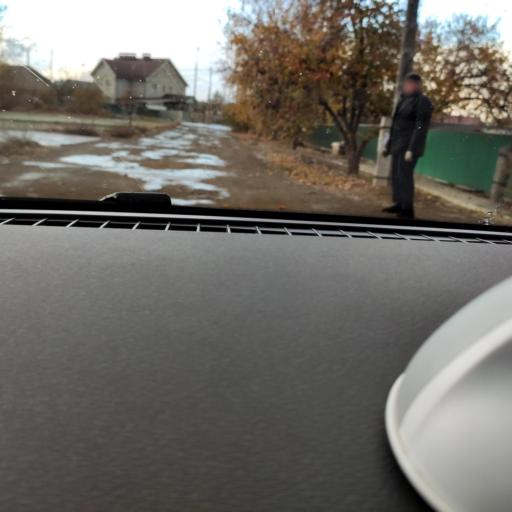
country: RU
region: Samara
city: Smyshlyayevka
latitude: 53.2333
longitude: 50.3129
